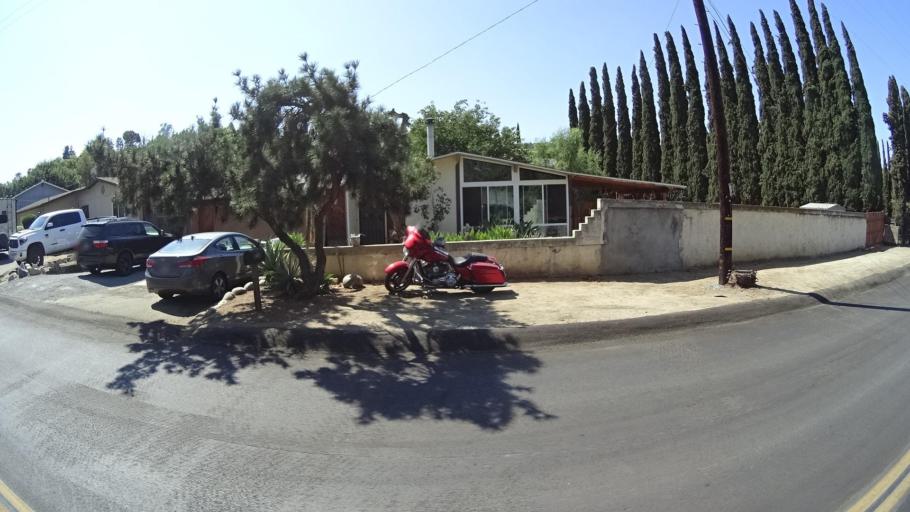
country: US
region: California
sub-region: San Diego County
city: Winter Gardens
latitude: 32.8387
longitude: -116.9304
